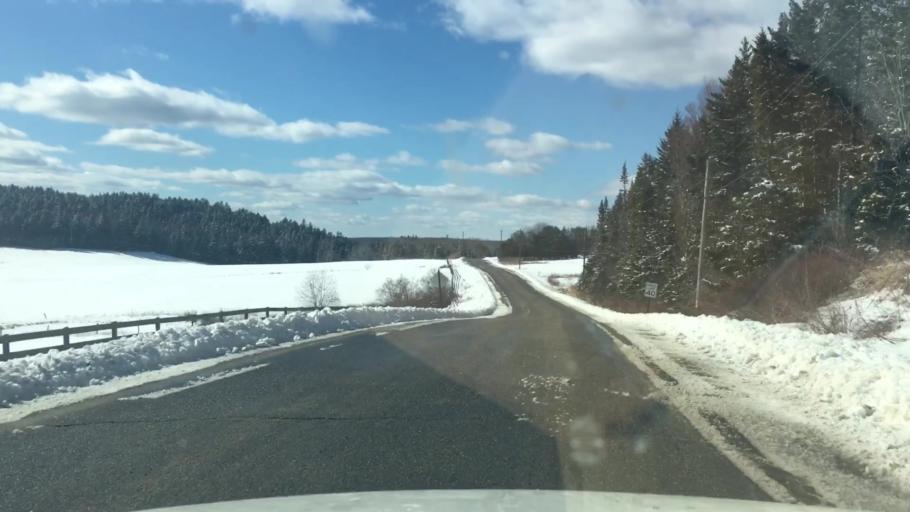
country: US
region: Maine
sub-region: Washington County
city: Machiasport
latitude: 44.6698
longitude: -67.4338
